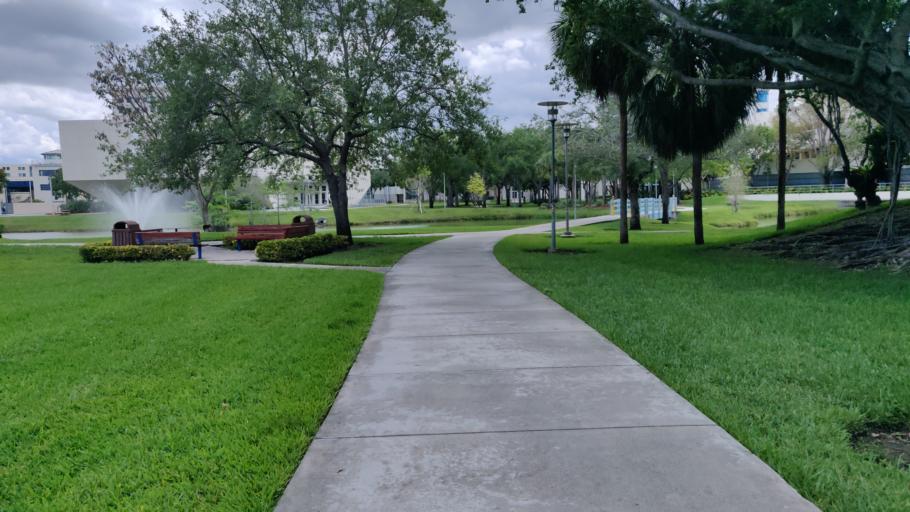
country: US
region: Florida
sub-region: Miami-Dade County
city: Sweetwater
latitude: 25.7570
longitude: -80.3748
